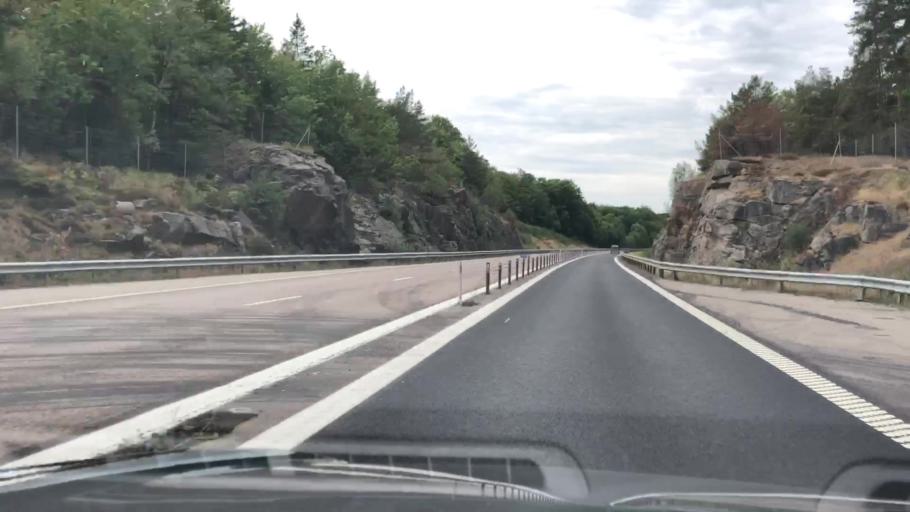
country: SE
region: Blekinge
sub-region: Ronneby Kommun
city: Brakne-Hoby
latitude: 56.2084
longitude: 15.0783
